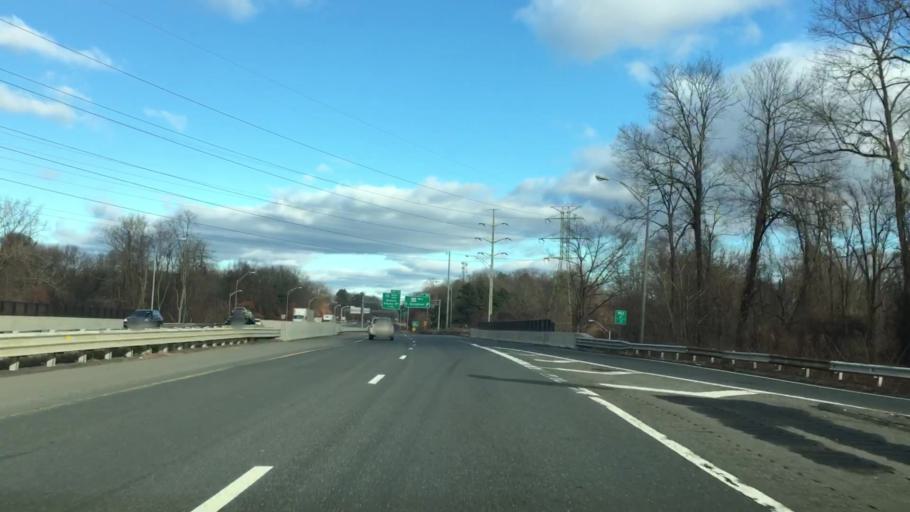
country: US
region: Massachusetts
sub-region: Hampden County
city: Chicopee
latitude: 42.1447
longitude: -72.5493
